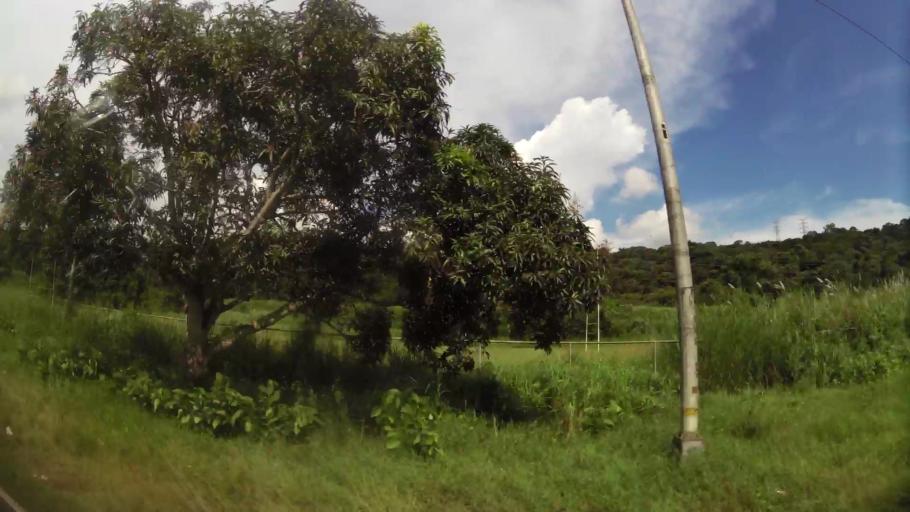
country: PA
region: Panama
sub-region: Distrito de Panama
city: Paraiso
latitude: 9.0280
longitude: -79.6214
